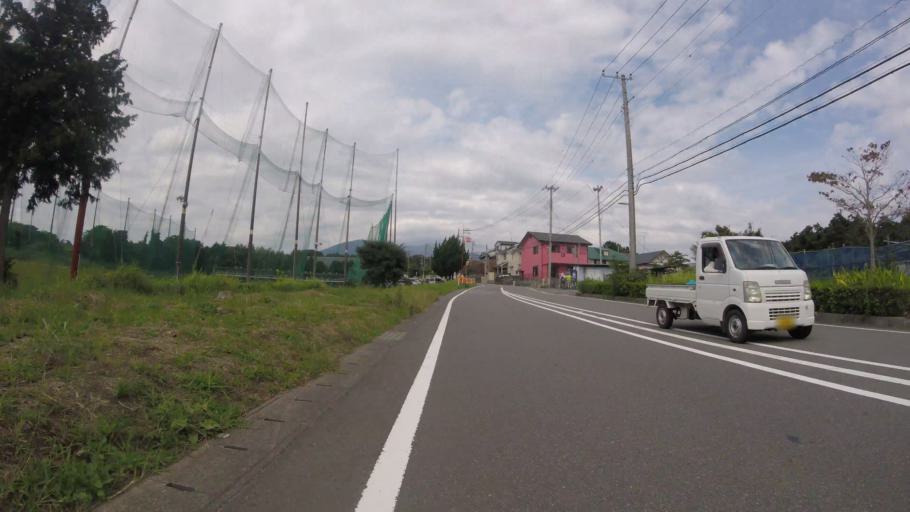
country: JP
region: Shizuoka
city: Numazu
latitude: 35.1376
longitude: 138.8574
